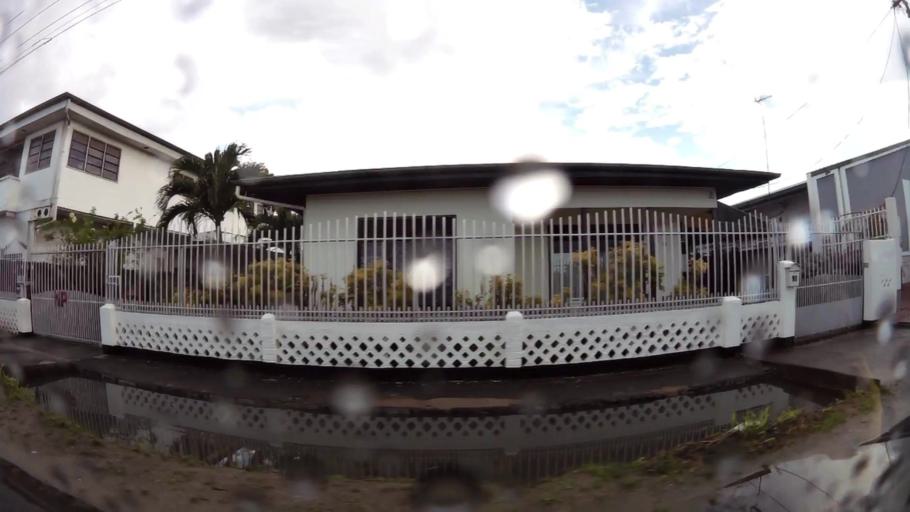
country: SR
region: Paramaribo
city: Paramaribo
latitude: 5.8271
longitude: -55.1838
